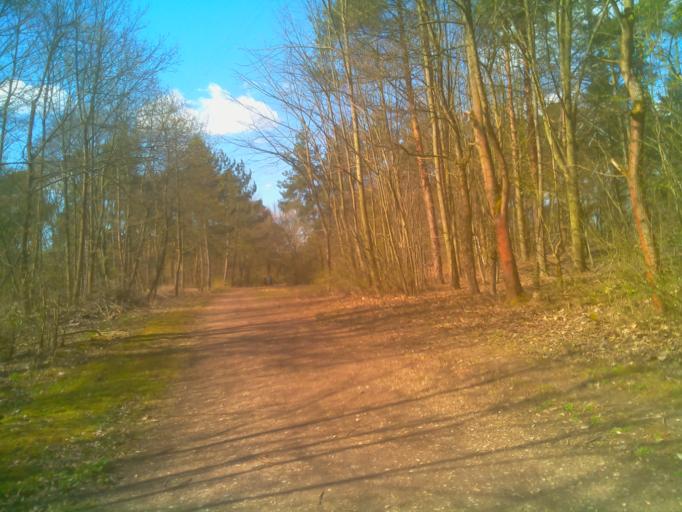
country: DE
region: Baden-Wuerttemberg
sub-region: Karlsruhe Region
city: Ilvesheim
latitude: 49.4462
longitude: 8.5377
